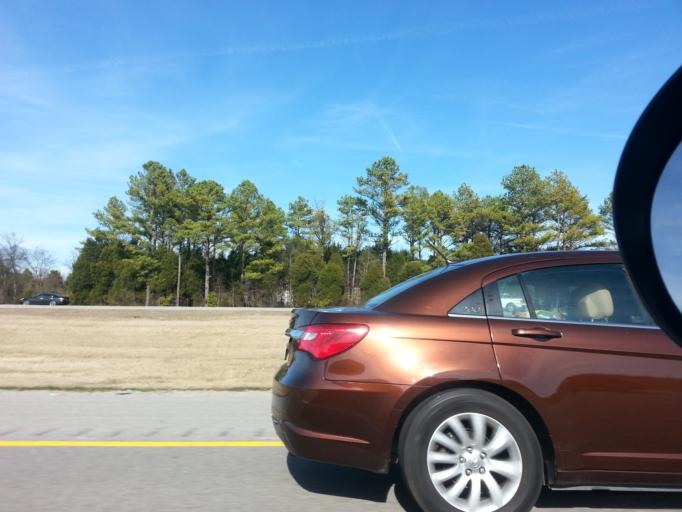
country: US
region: Tennessee
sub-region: Rutherford County
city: Smyrna
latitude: 35.9491
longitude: -86.5484
